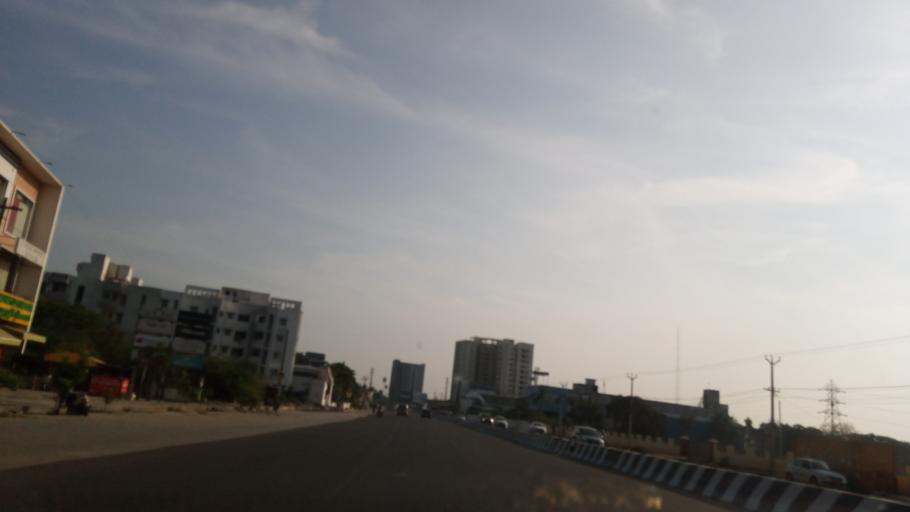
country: IN
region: Tamil Nadu
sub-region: Kancheepuram
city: Poonamalle
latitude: 13.0511
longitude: 80.1225
